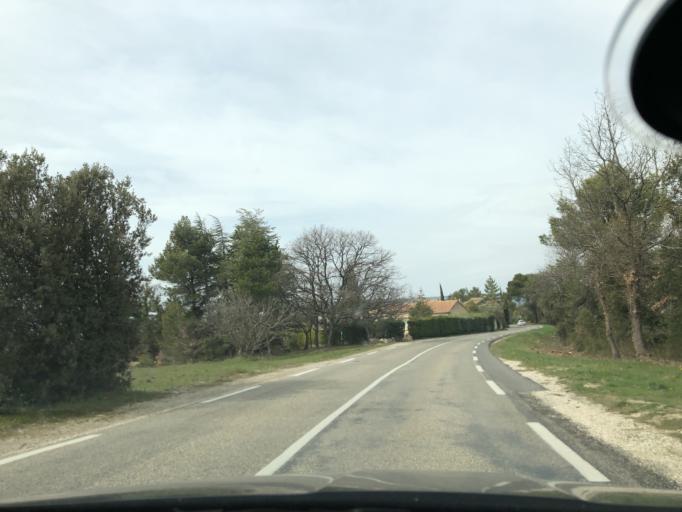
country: FR
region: Provence-Alpes-Cote d'Azur
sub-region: Departement du Vaucluse
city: Goult
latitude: 43.8324
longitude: 5.2380
